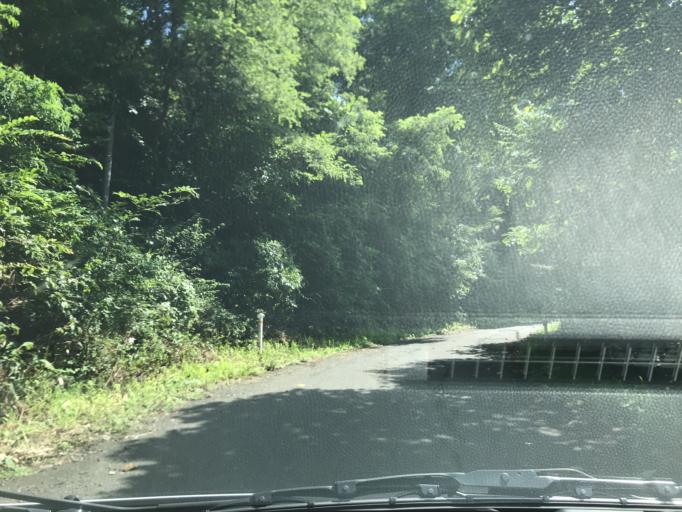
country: JP
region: Iwate
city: Ofunato
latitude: 38.9879
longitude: 141.4286
